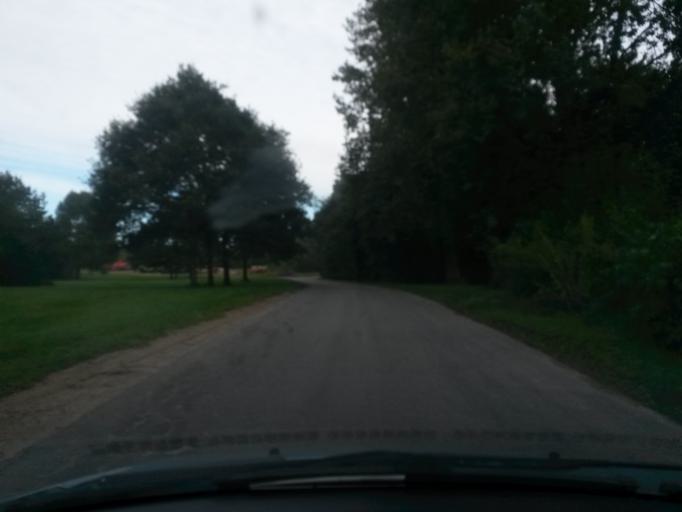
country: DK
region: Central Jutland
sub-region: Silkeborg Kommune
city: Kjellerup
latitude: 56.2910
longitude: 9.4371
